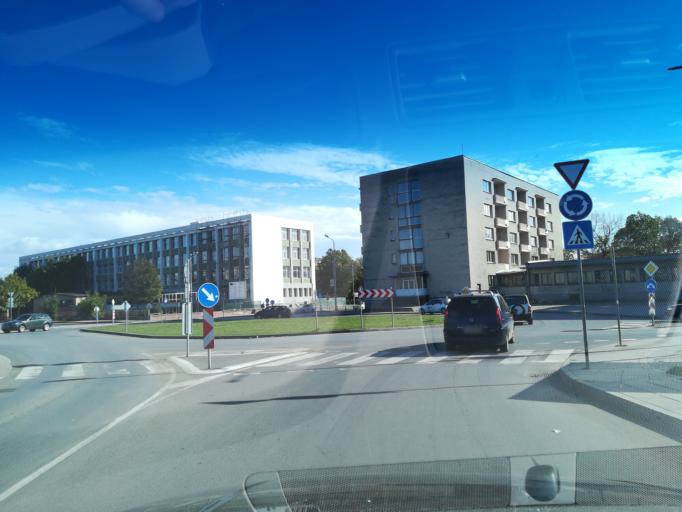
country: BG
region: Stara Zagora
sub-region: Obshtina Stara Zagora
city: Stara Zagora
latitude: 42.4312
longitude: 25.6394
